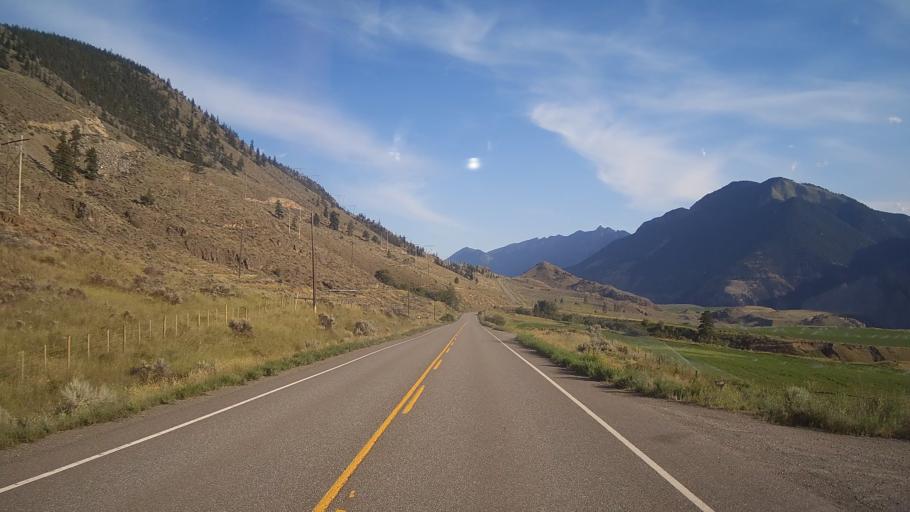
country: CA
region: British Columbia
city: Lillooet
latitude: 50.8492
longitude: -121.8620
